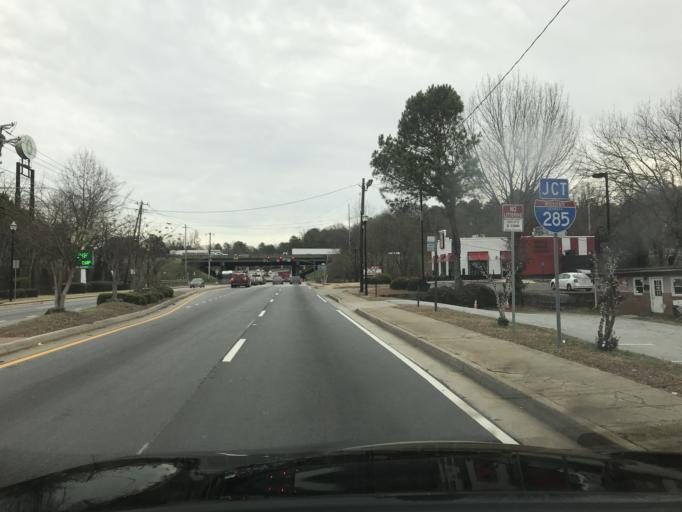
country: US
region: Georgia
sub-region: Fulton County
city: East Point
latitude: 33.7230
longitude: -84.5046
